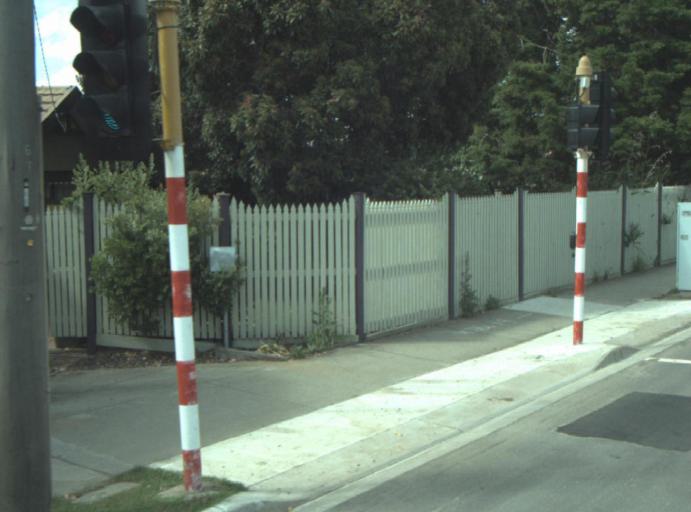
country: AU
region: Victoria
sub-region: Greater Geelong
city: Breakwater
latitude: -38.1781
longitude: 144.3395
